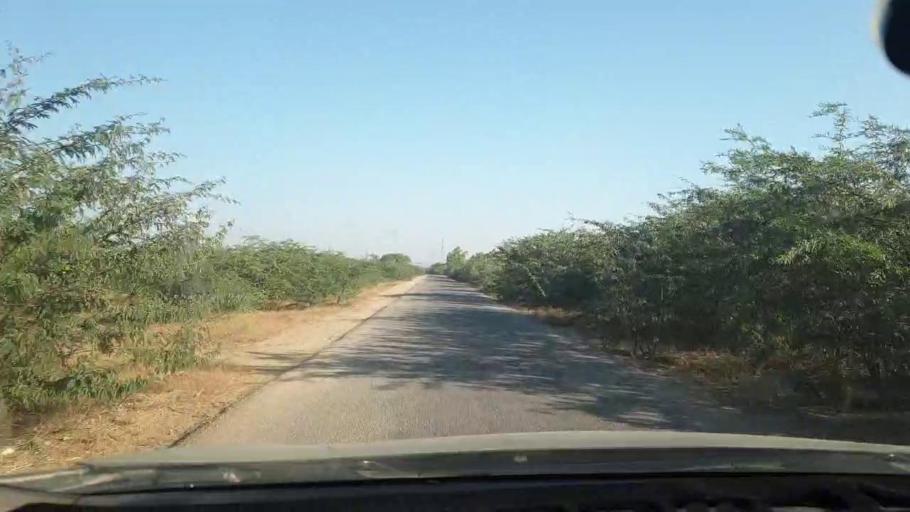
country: PK
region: Sindh
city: Malir Cantonment
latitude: 25.1514
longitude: 67.1899
